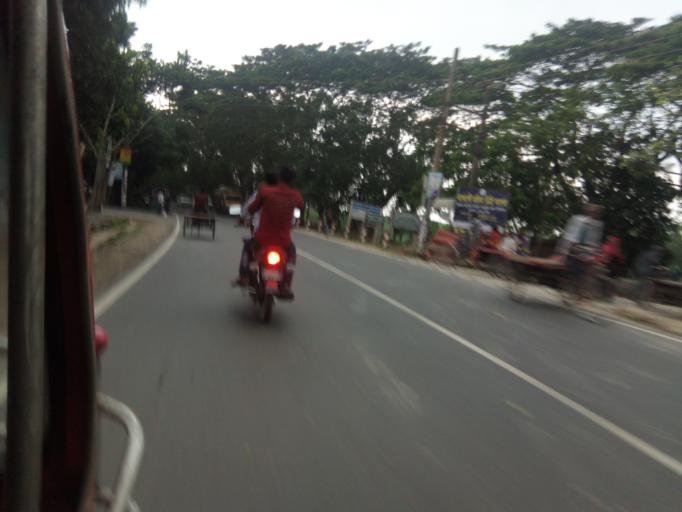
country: BD
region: Khulna
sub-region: Magura
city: Magura
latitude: 23.5421
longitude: 89.6225
